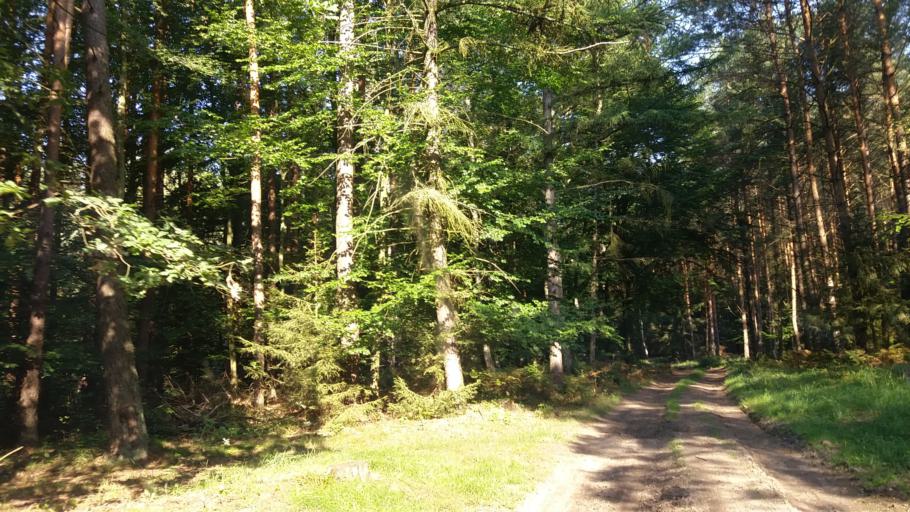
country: PL
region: West Pomeranian Voivodeship
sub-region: Powiat choszczenski
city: Pelczyce
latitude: 52.9691
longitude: 15.3580
